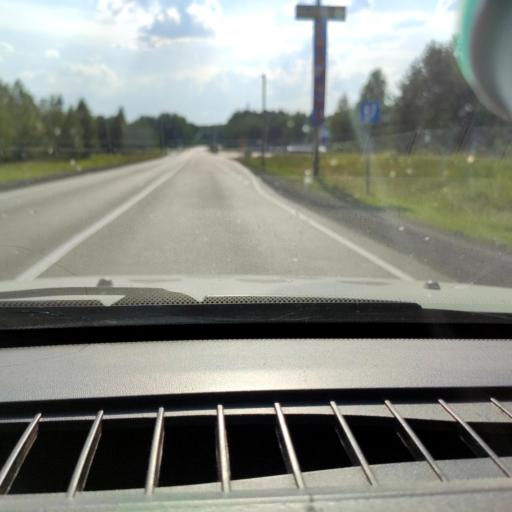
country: RU
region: Udmurtiya
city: Debesy
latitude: 57.7218
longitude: 54.1417
